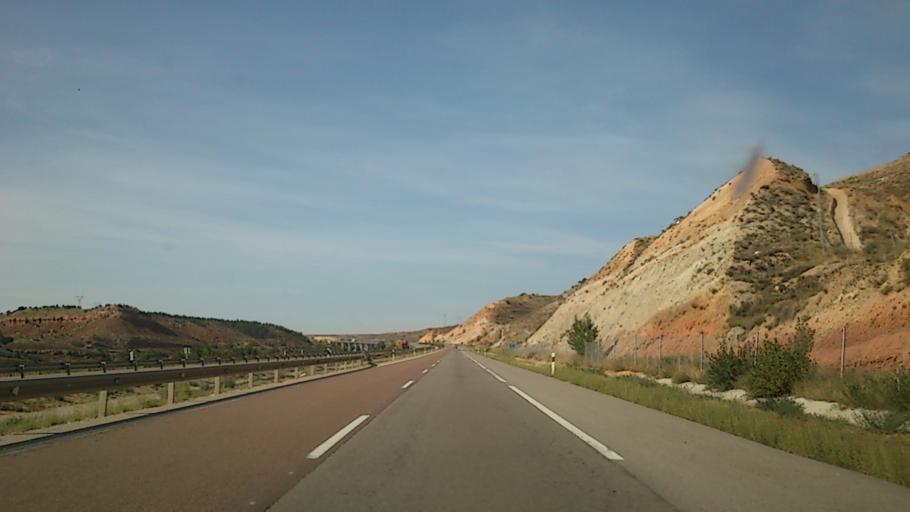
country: ES
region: Aragon
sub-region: Provincia de Teruel
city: Calamocha
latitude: 40.9805
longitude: -1.2596
